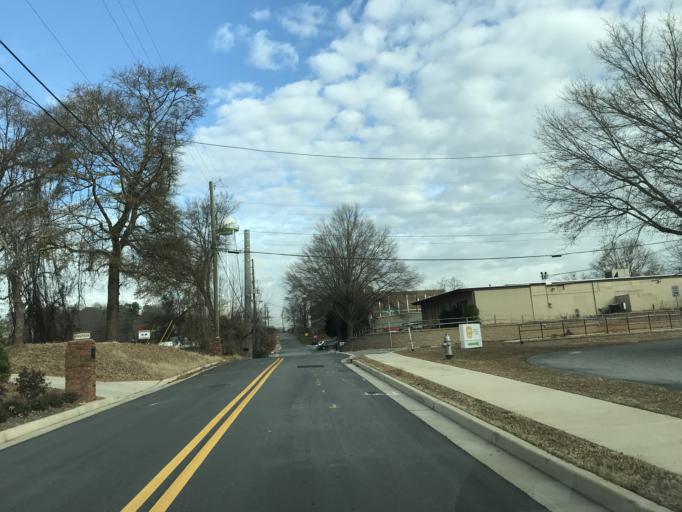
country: US
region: Georgia
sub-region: Fulton County
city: Roswell
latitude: 34.0185
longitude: -84.3601
